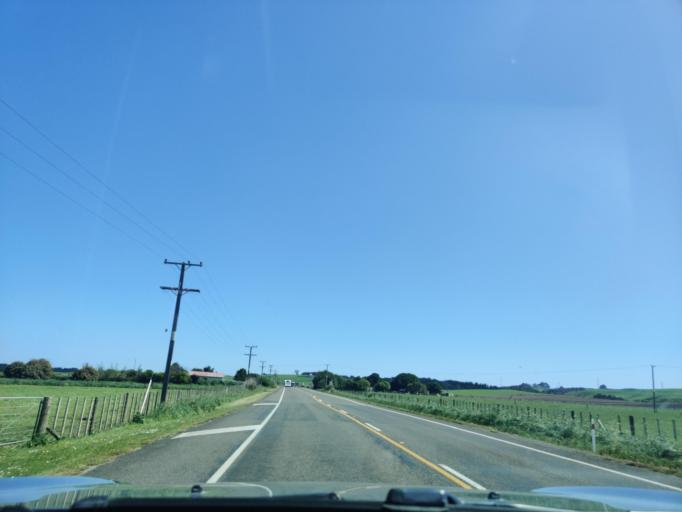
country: NZ
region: Manawatu-Wanganui
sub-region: Wanganui District
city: Wanganui
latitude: -39.8180
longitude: 174.8327
